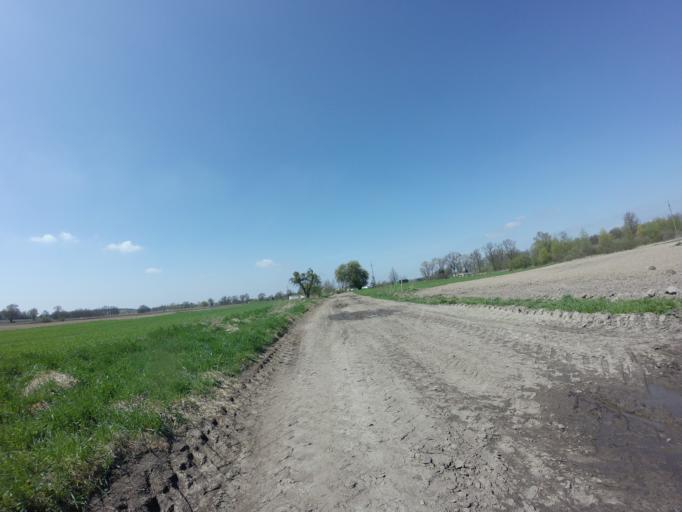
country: PL
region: West Pomeranian Voivodeship
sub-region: Powiat choszczenski
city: Choszczno
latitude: 53.1679
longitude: 15.4668
